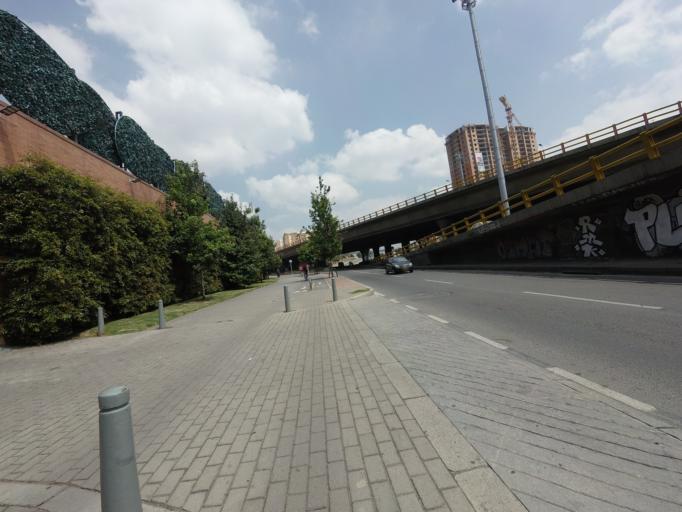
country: CO
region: Bogota D.C.
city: Barrio San Luis
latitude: 4.7212
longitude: -74.0751
